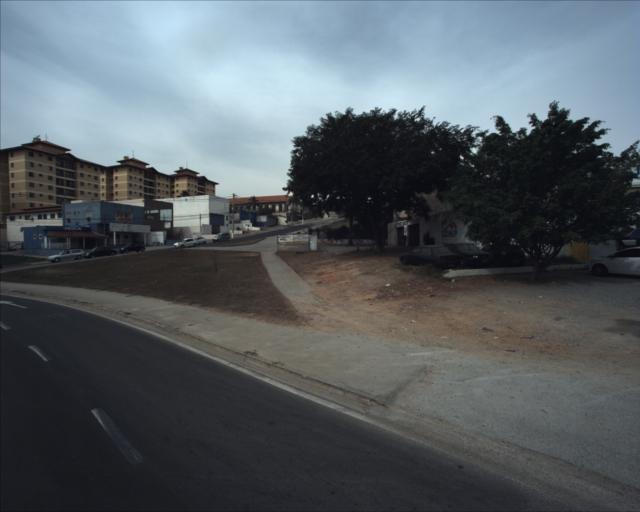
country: BR
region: Sao Paulo
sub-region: Sorocaba
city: Sorocaba
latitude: -23.4814
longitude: -47.4583
